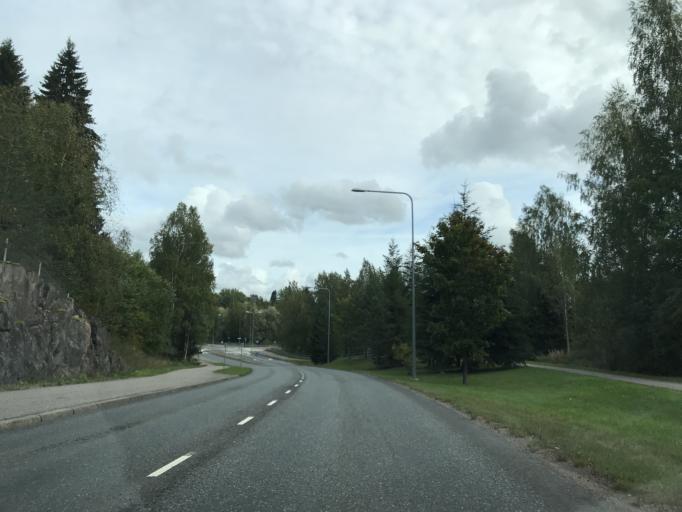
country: FI
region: Paijanne Tavastia
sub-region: Lahti
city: Lahti
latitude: 60.9915
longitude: 25.7446
